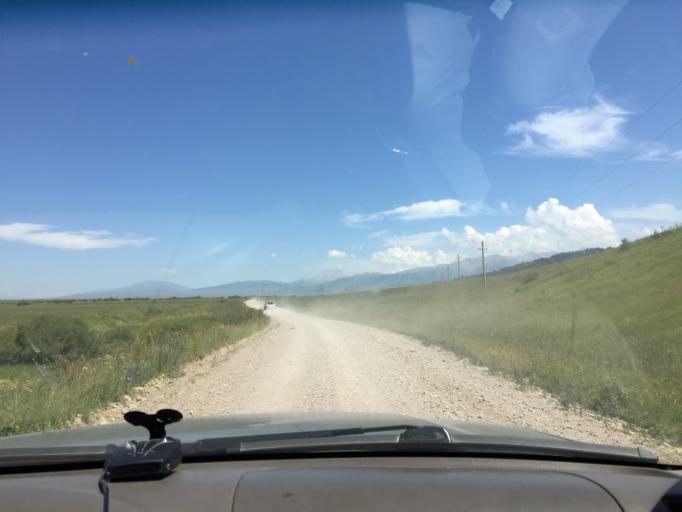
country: KZ
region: Almaty Oblysy
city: Kegen
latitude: 42.7656
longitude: 79.1108
